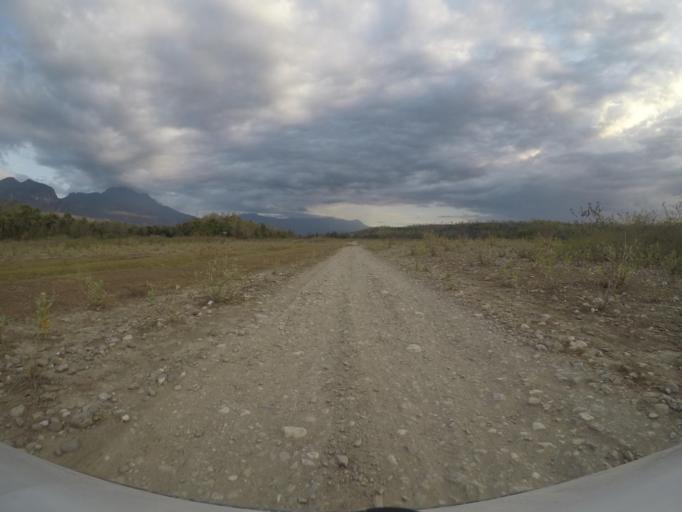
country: TL
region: Bobonaro
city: Maliana
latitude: -8.8938
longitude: 125.2086
